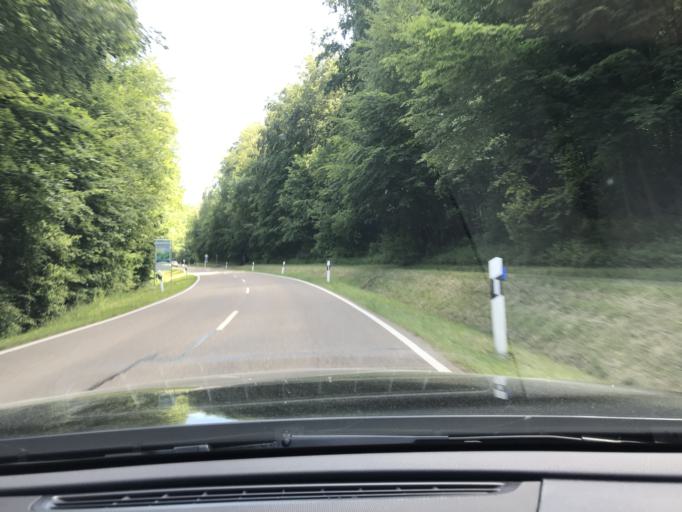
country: DE
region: Baden-Wuerttemberg
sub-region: Regierungsbezirk Stuttgart
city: Weinstadt-Endersbach
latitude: 48.7883
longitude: 9.3870
